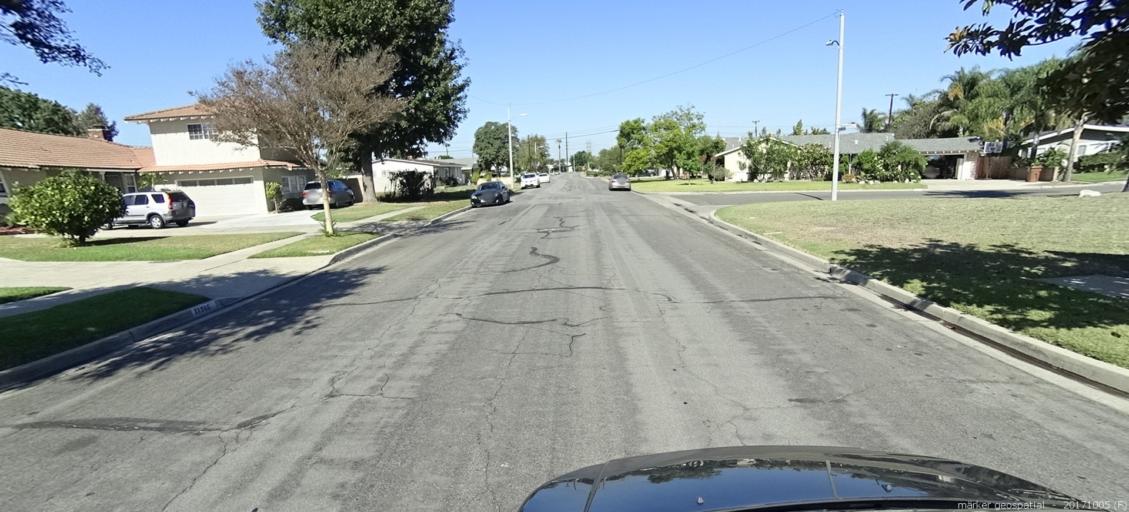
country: US
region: California
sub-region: Orange County
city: Stanton
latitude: 33.7992
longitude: -117.9815
